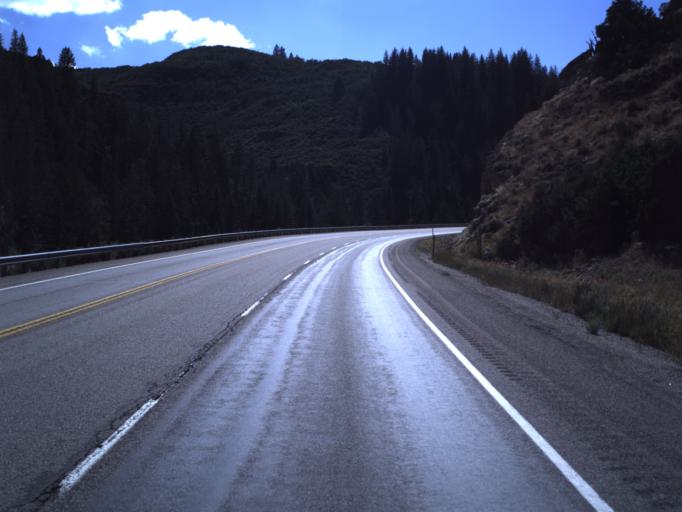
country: US
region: Utah
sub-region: Carbon County
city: Helper
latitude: 40.1948
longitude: -110.9330
